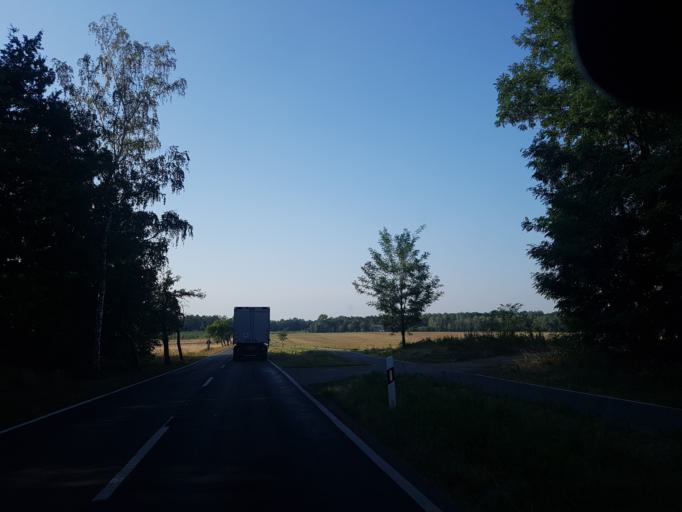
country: DE
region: Brandenburg
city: Hohenleipisch
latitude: 51.4806
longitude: 13.5479
